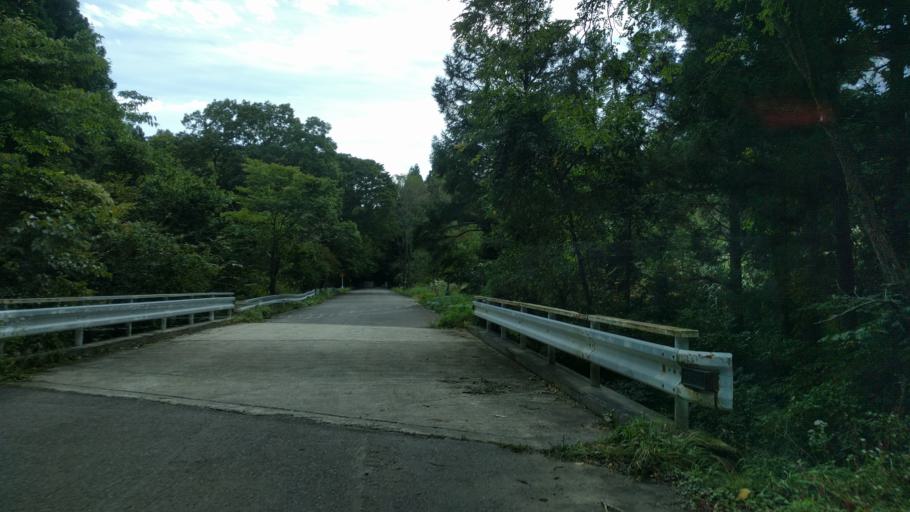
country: JP
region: Fukushima
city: Inawashiro
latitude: 37.3761
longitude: 140.1574
